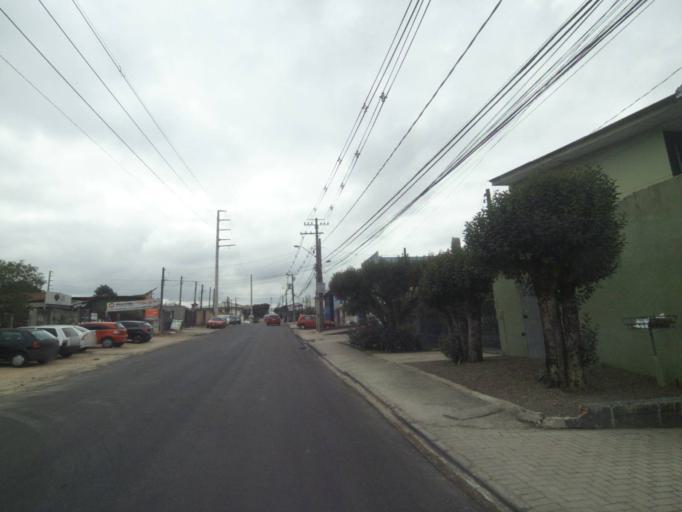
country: BR
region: Parana
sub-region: Sao Jose Dos Pinhais
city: Sao Jose dos Pinhais
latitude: -25.5439
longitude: -49.2754
